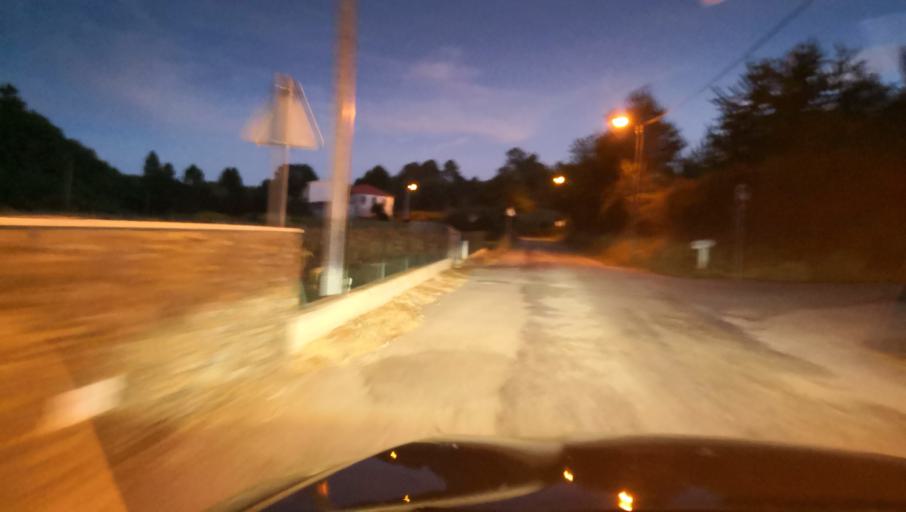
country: PT
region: Vila Real
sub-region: Sabrosa
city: Vilela
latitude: 41.2609
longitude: -7.6494
